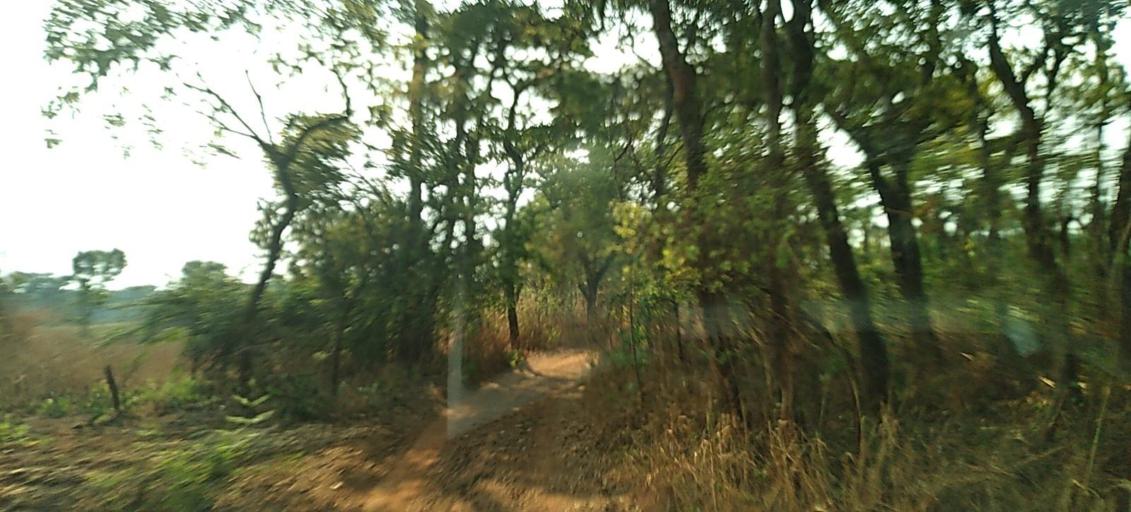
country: ZM
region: North-Western
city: Solwezi
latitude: -12.0593
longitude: 26.1652
